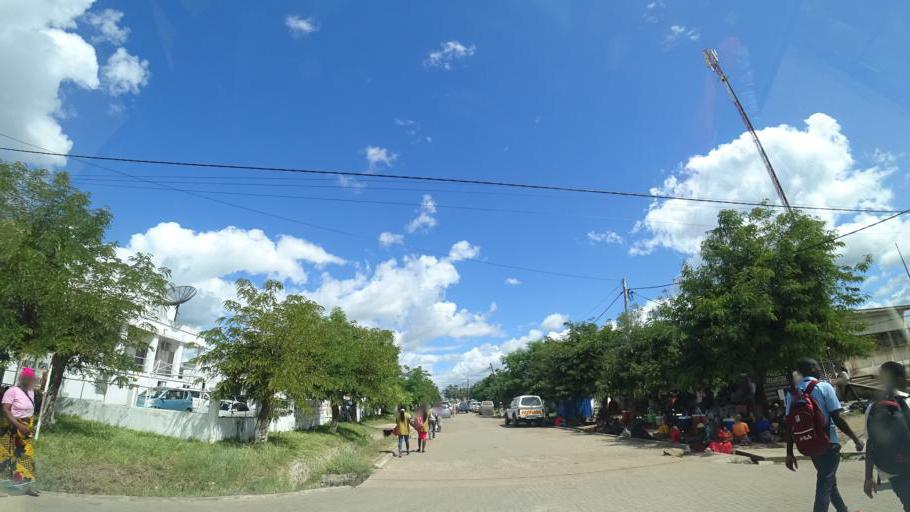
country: MZ
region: Sofala
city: Dondo
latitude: -19.2724
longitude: 34.2051
